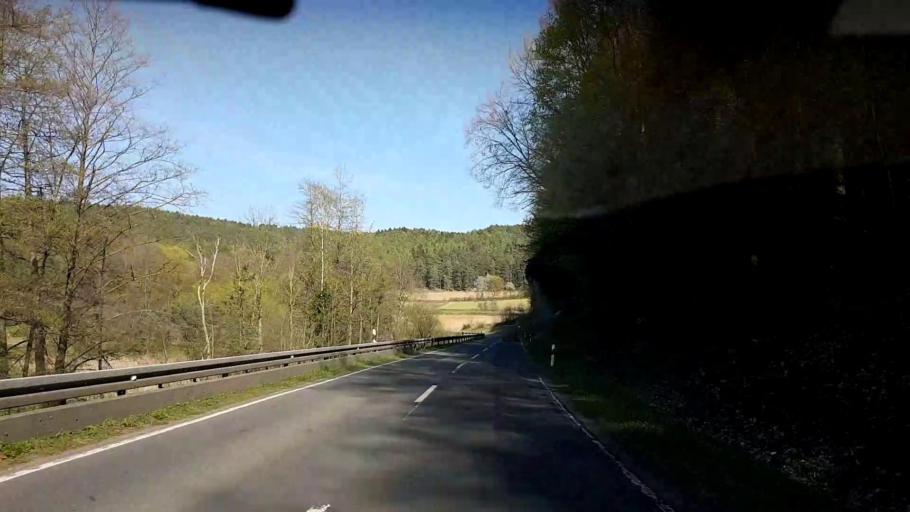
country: DE
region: Bavaria
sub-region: Upper Franconia
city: Plankenfels
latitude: 49.8749
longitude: 11.3386
